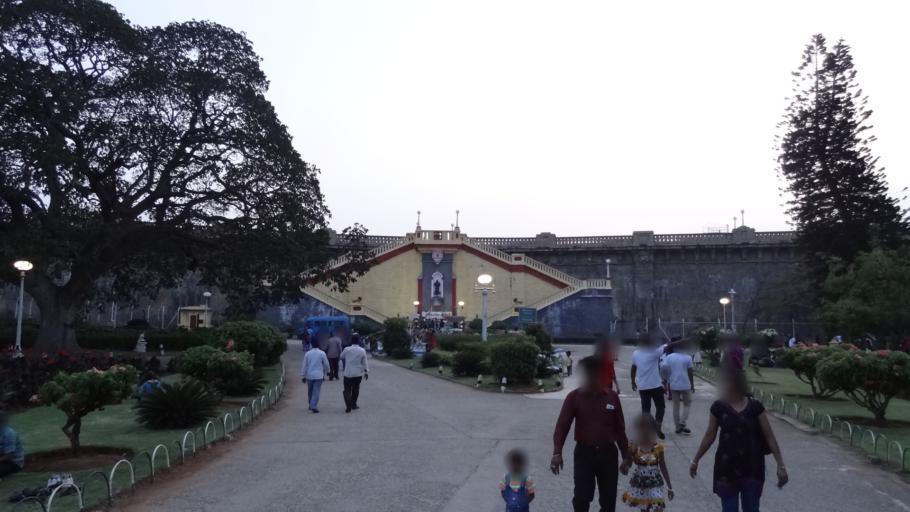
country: IN
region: Karnataka
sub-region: Mandya
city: Shrirangapattana
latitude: 12.4196
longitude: 76.5724
